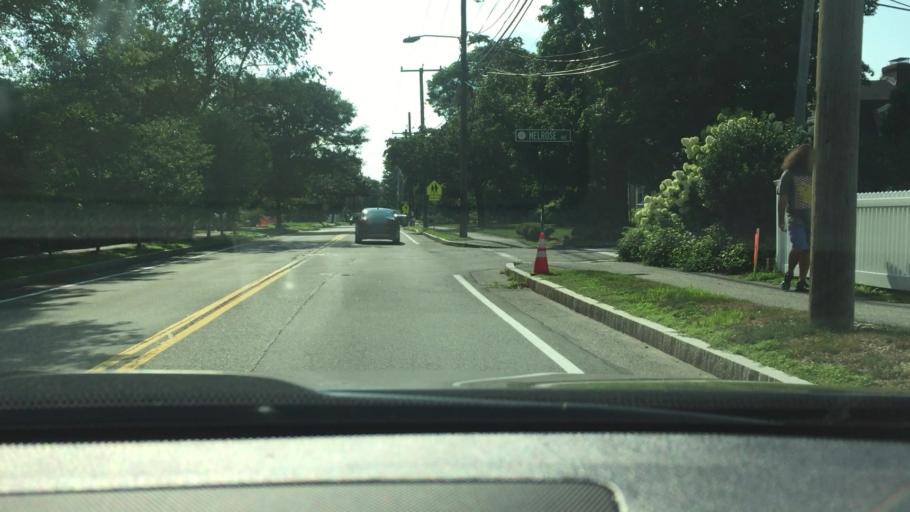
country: US
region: Massachusetts
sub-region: Norfolk County
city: Needham
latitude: 42.2804
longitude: -71.2235
